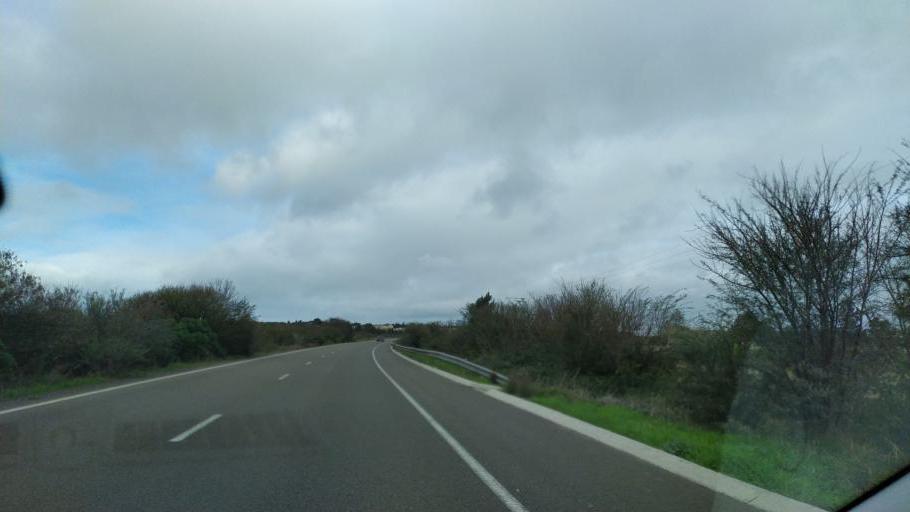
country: MA
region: Gharb-Chrarda-Beni Hssen
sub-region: Kenitra Province
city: Kenitra
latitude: 34.4115
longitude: -6.5240
